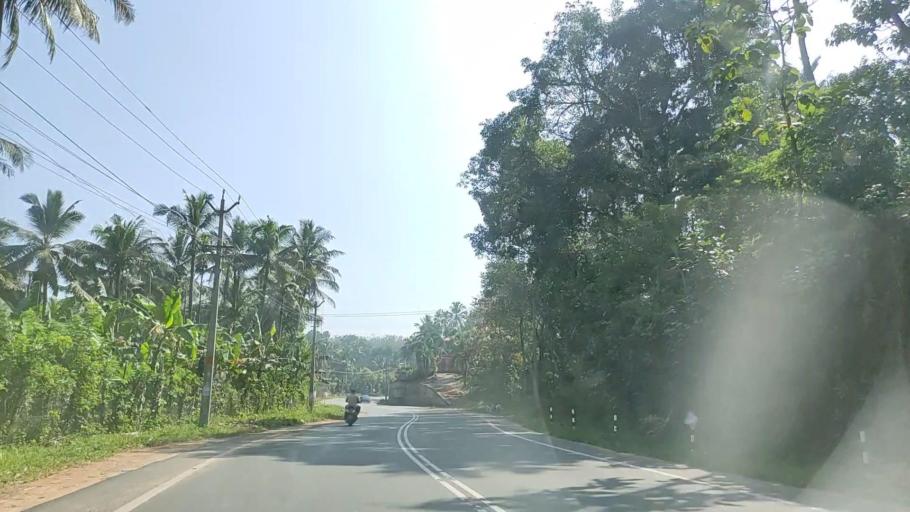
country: IN
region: Kerala
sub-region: Kollam
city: Punalur
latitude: 8.9309
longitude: 76.9683
